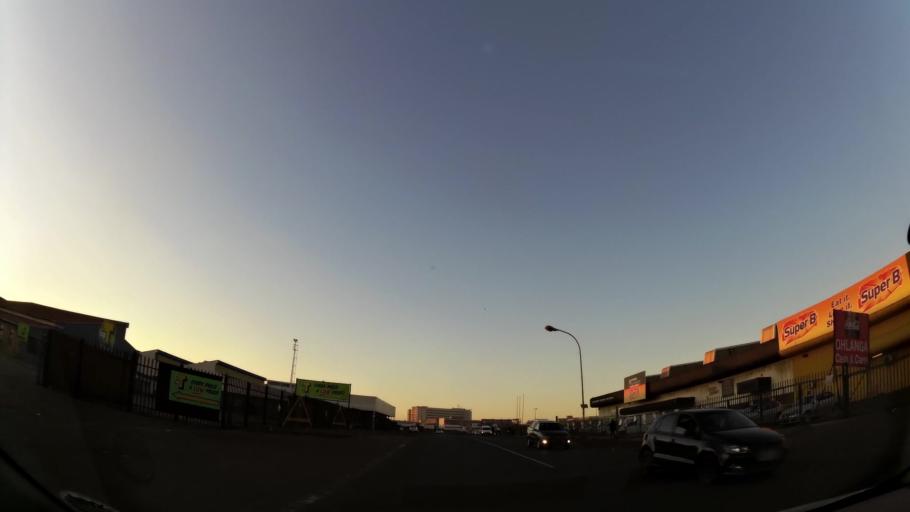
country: ZA
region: Mpumalanga
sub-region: Nkangala District Municipality
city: Witbank
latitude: -25.8788
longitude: 29.2080
